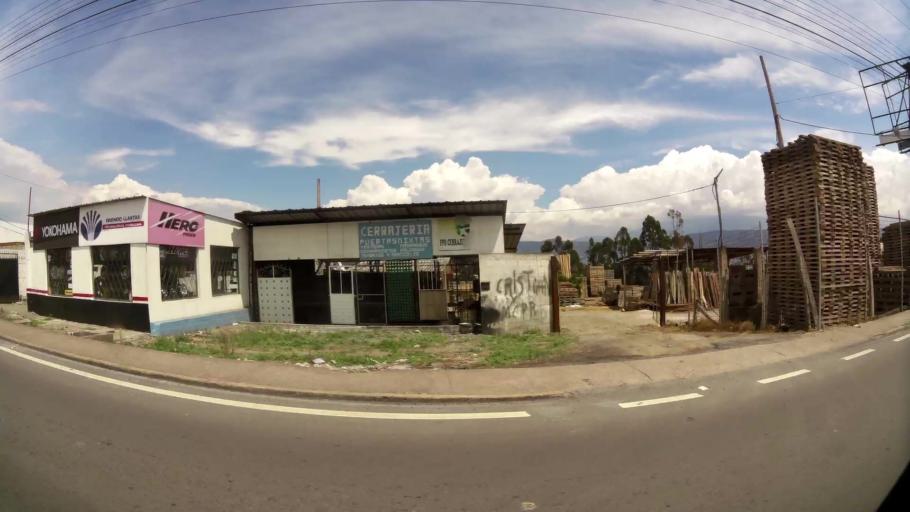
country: EC
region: Pichincha
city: Sangolqui
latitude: -0.2045
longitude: -78.3678
